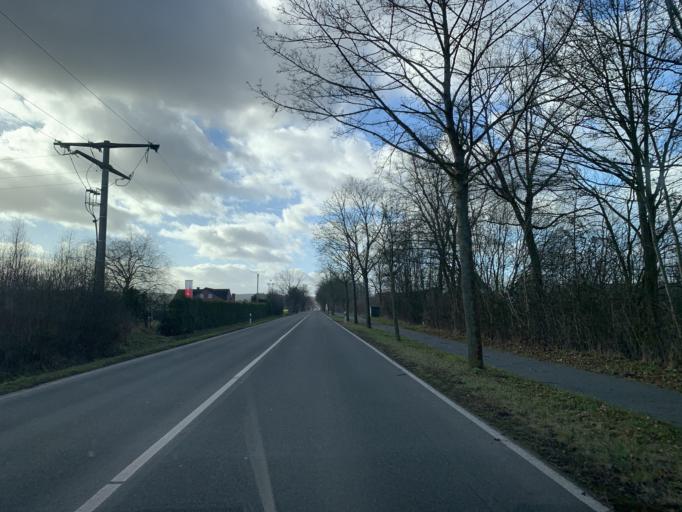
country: DE
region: North Rhine-Westphalia
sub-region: Regierungsbezirk Munster
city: Havixbeck
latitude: 51.9818
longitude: 7.4386
